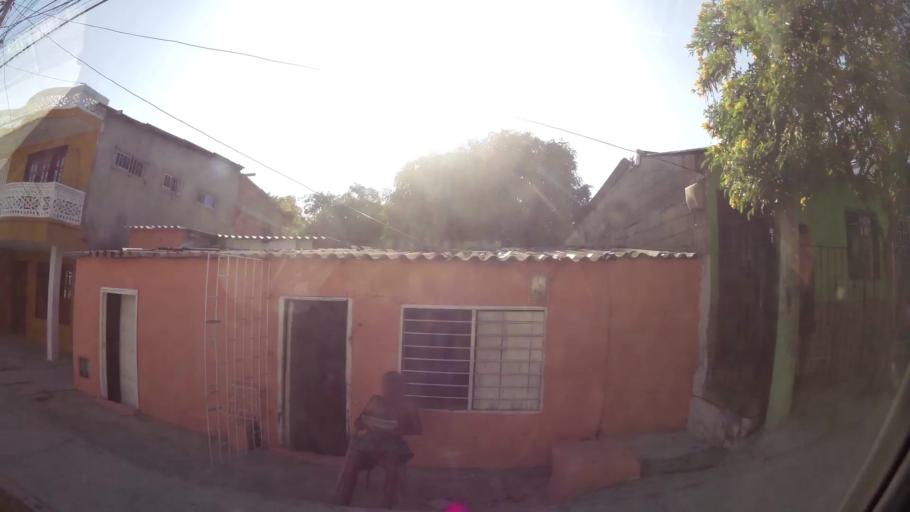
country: CO
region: Bolivar
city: Cartagena
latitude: 10.4019
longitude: -75.4859
